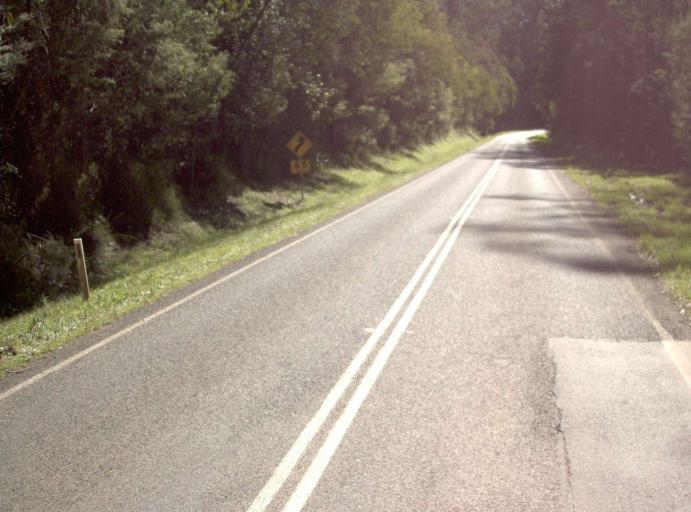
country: AU
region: Victoria
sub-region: Yarra Ranges
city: Millgrove
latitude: -37.8726
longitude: 145.8186
